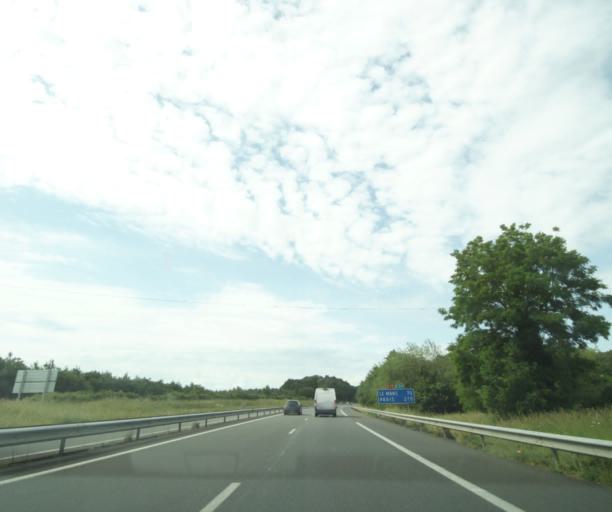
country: FR
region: Pays de la Loire
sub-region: Departement de Maine-et-Loire
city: Seiches-sur-le-Loir
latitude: 47.5731
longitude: -0.3347
